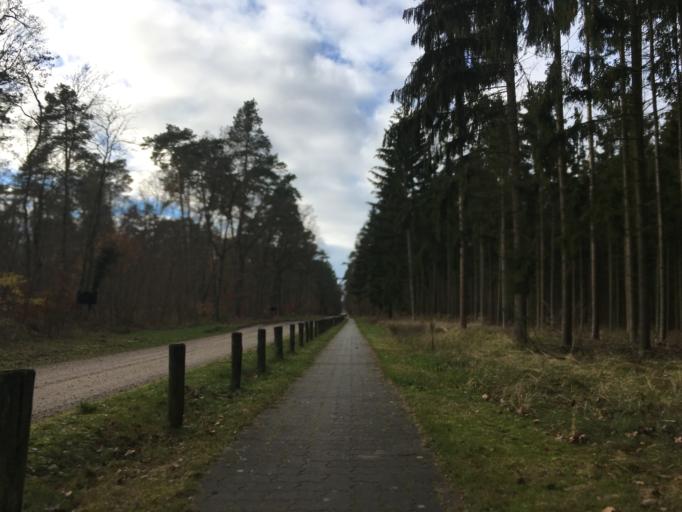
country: DE
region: Brandenburg
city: Waldsieversdorf
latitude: 52.5486
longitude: 14.0809
